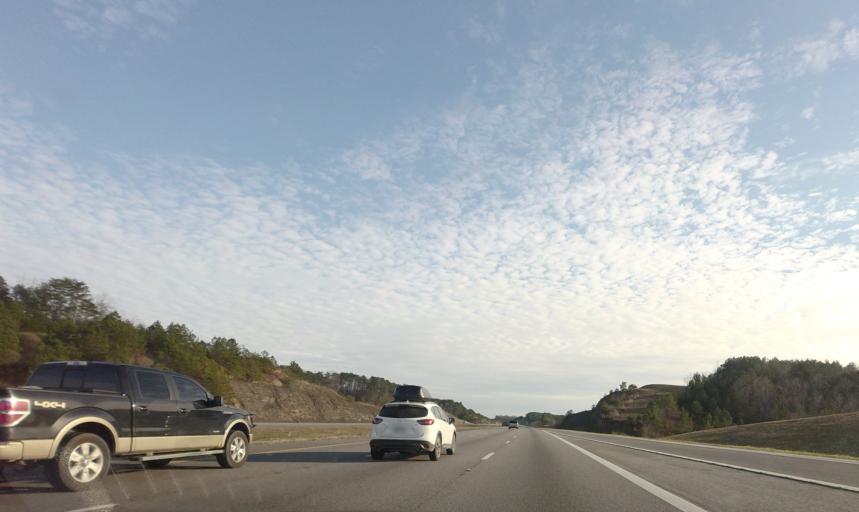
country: US
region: Alabama
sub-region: Walker County
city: Cordova
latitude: 33.7373
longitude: -87.1986
